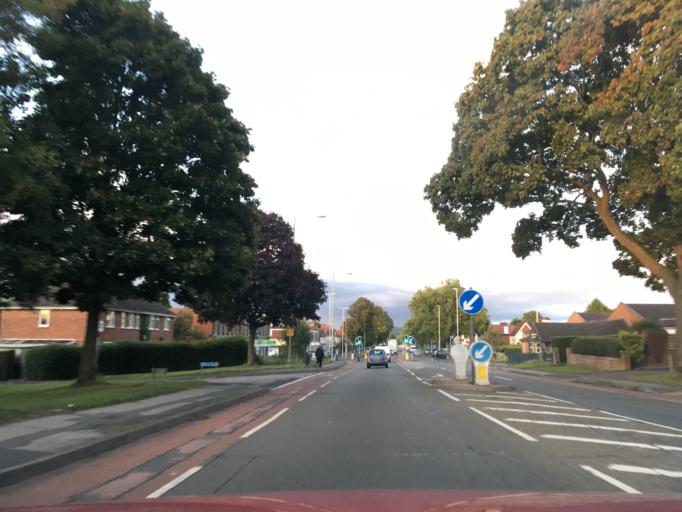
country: GB
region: England
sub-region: Gloucestershire
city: Gloucester
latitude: 51.8433
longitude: -2.2377
